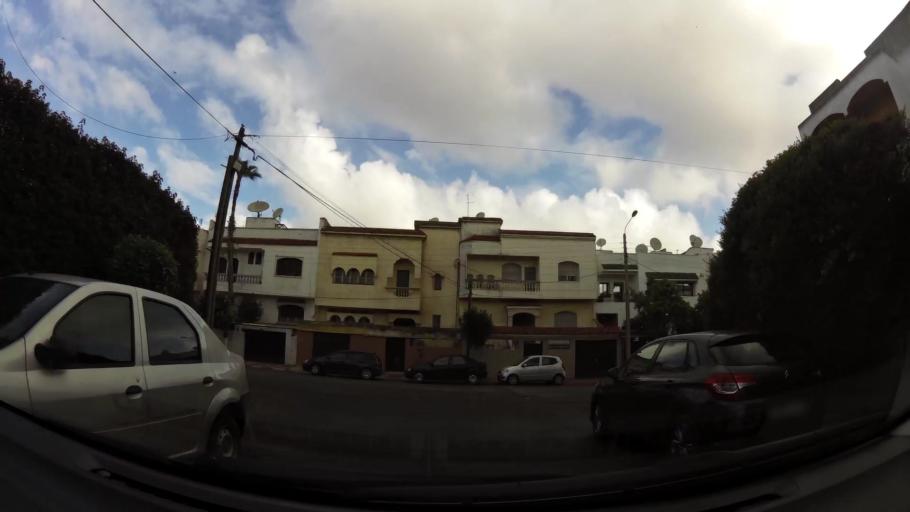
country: MA
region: Grand Casablanca
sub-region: Casablanca
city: Casablanca
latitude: 33.5627
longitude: -7.6809
